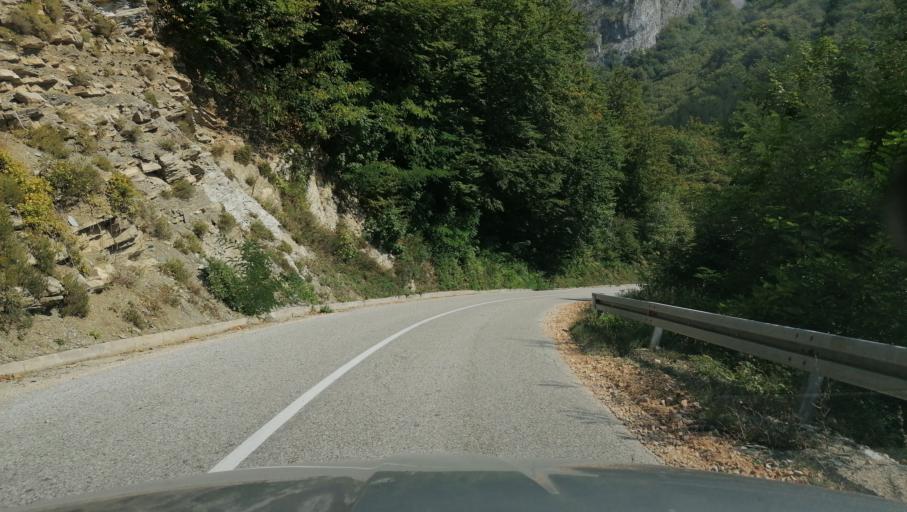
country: BA
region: Republika Srpska
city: Gacko
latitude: 43.2982
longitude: 18.6402
